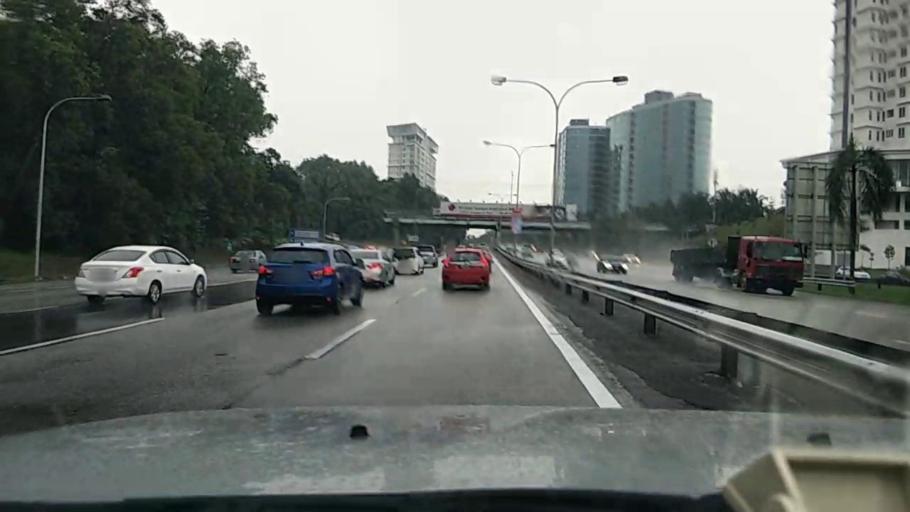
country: MY
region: Kuala Lumpur
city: Kuala Lumpur
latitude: 3.1038
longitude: 101.6946
